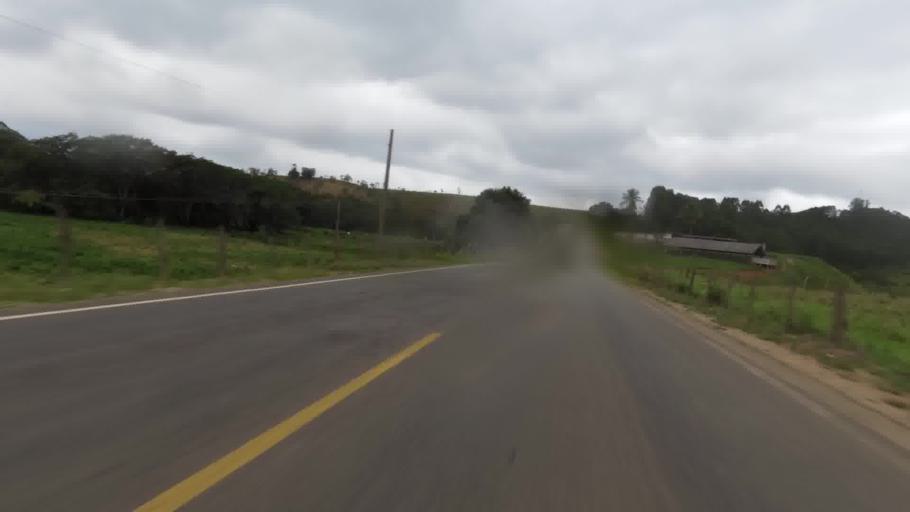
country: BR
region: Espirito Santo
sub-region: Alfredo Chaves
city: Alfredo Chaves
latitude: -20.6608
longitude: -40.7437
